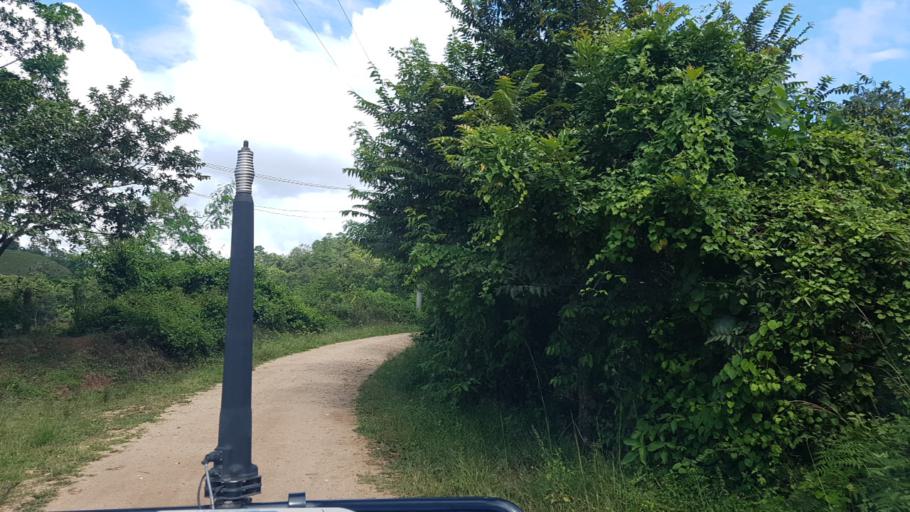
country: NI
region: Nueva Segovia
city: Ciudad Antigua
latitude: 13.6508
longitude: -86.2490
